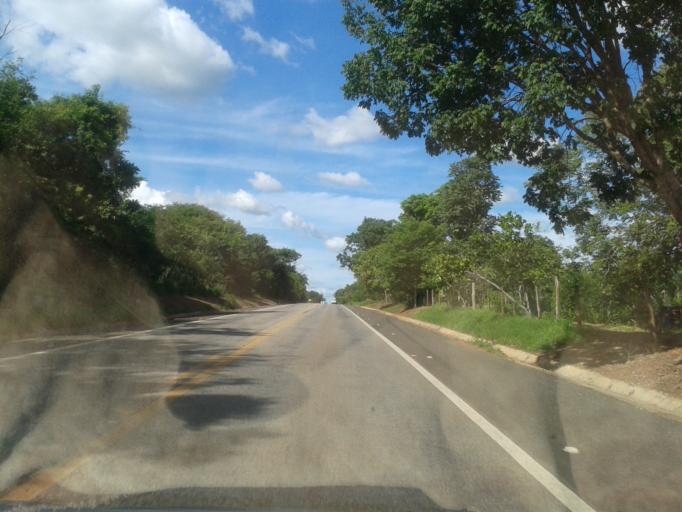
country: BR
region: Goias
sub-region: Mozarlandia
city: Mozarlandia
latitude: -15.0671
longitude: -50.6166
